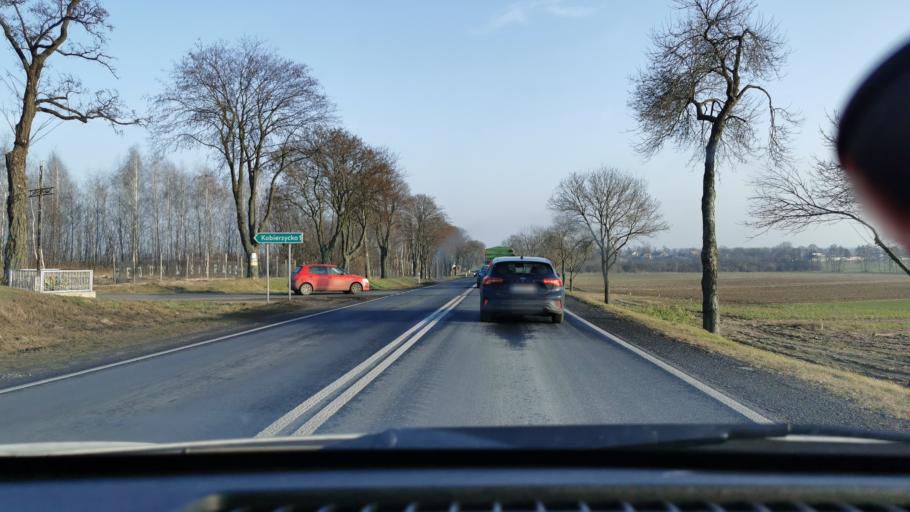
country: PL
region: Lodz Voivodeship
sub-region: Powiat sieradzki
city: Wroblew
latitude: 51.6160
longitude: 18.6012
